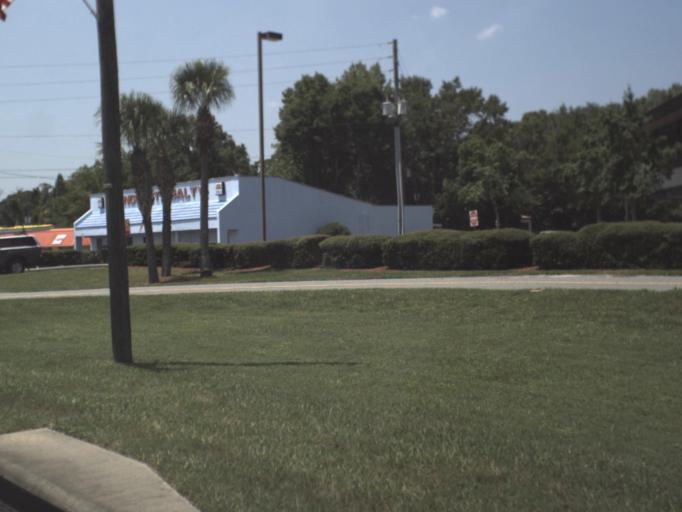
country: US
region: Florida
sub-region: Citrus County
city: Crystal River
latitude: 28.8861
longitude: -82.5840
